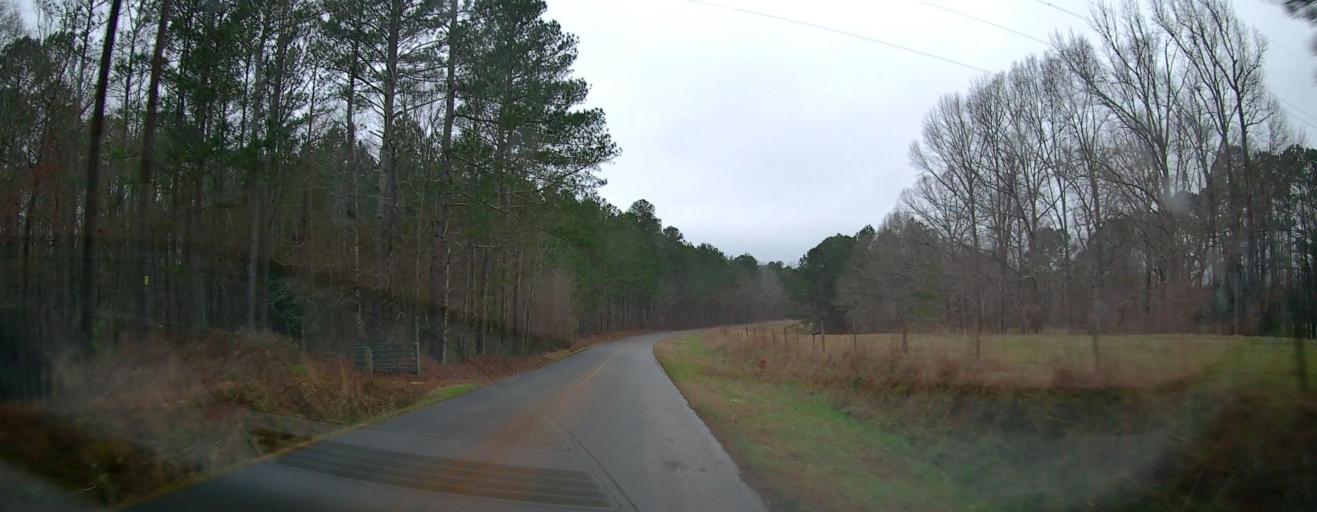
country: US
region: Georgia
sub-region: Monroe County
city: Forsyth
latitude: 33.0875
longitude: -83.9360
